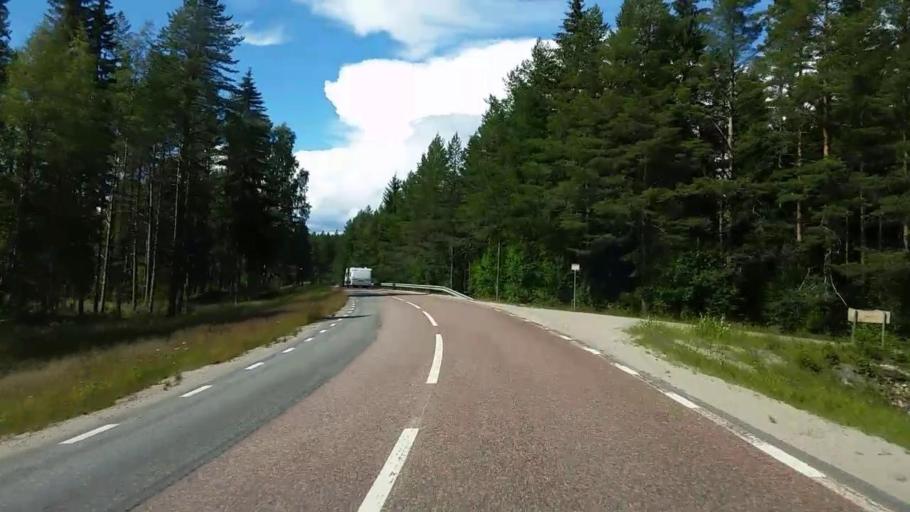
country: SE
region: Gaevleborg
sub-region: Ovanakers Kommun
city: Edsbyn
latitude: 61.3065
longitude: 15.5095
